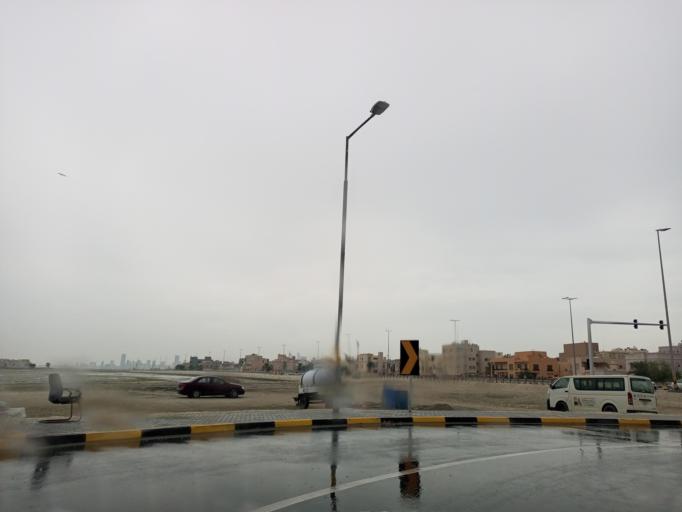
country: BH
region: Muharraq
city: Al Hadd
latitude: 26.2465
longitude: 50.6411
